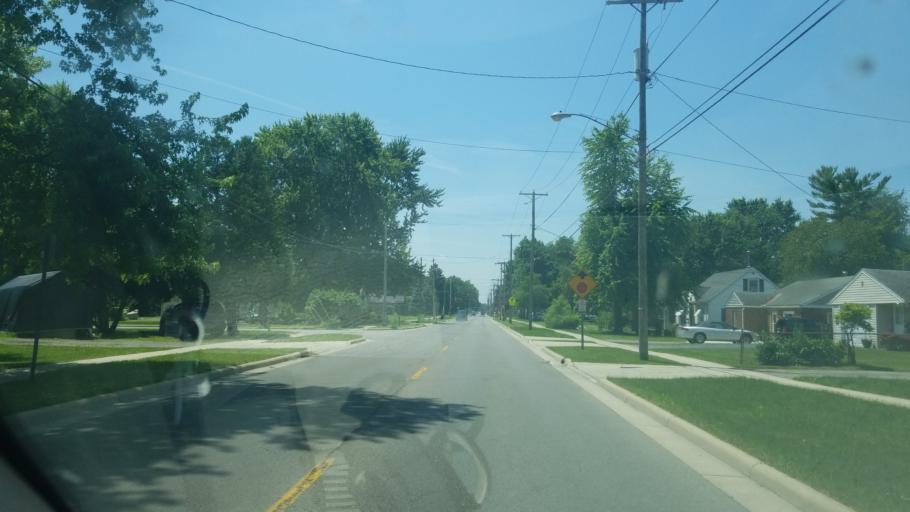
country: US
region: Ohio
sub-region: Hancock County
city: Findlay
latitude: 41.0594
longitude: -83.6369
